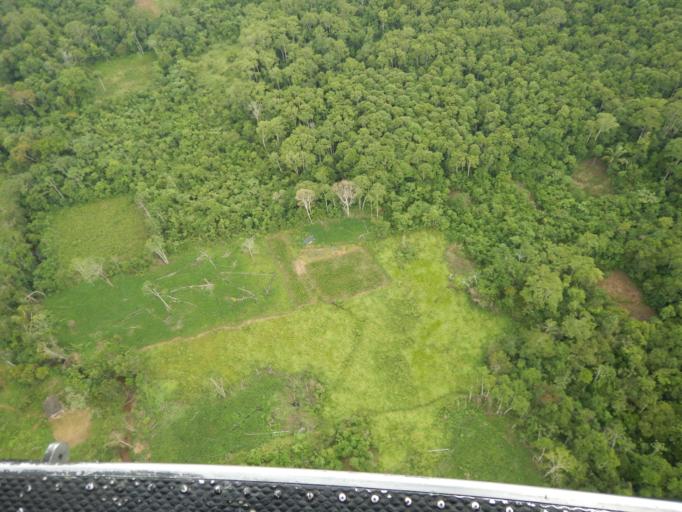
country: BO
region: Cochabamba
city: Chimore
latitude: -17.0036
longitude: -64.9108
